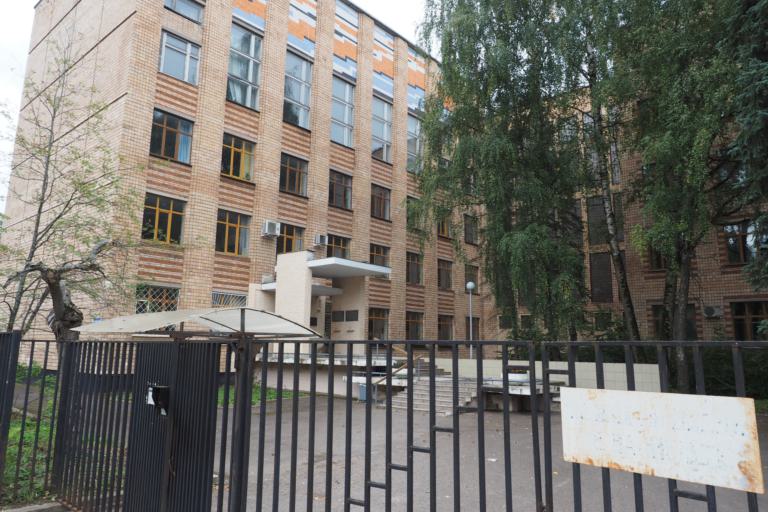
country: RU
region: Moskovskaya
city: Pushchino
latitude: 54.8320
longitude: 37.6096
